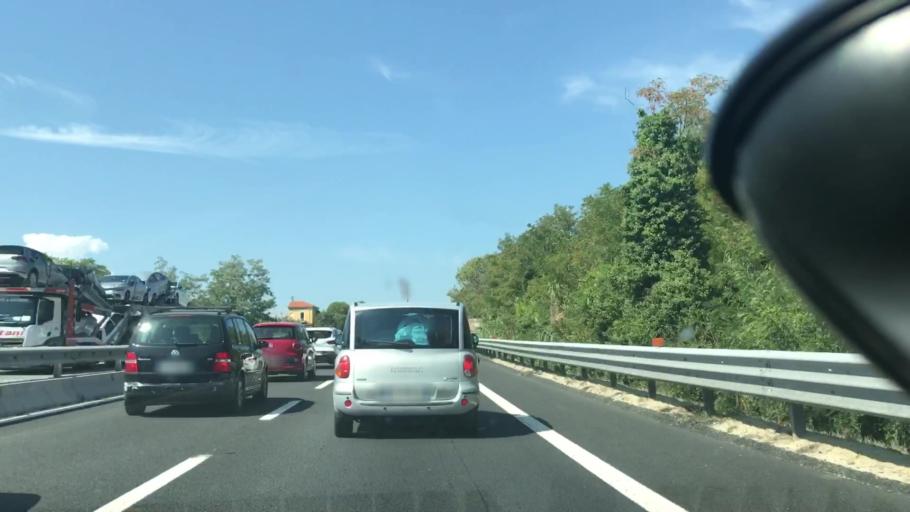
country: IT
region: Abruzzo
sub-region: Provincia di Chieti
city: Torino di Sangro
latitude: 42.2047
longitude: 14.5318
